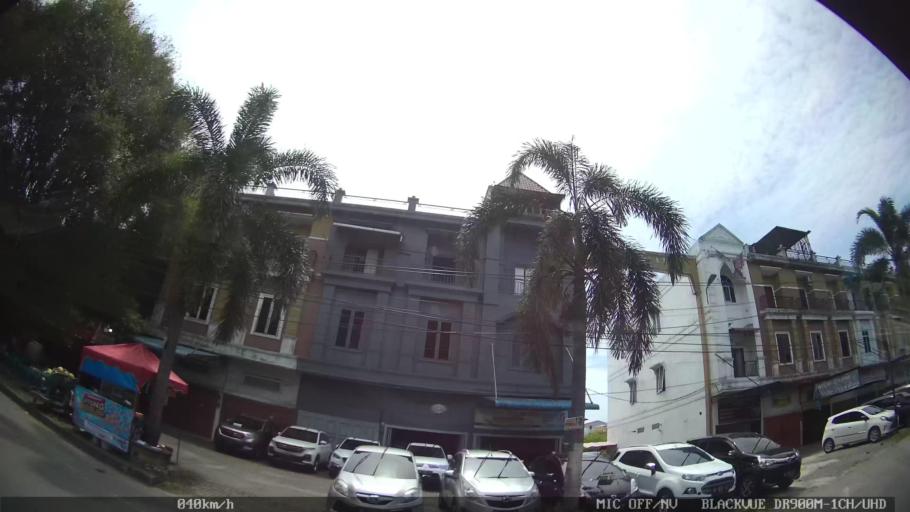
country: ID
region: North Sumatra
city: Sunggal
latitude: 3.5507
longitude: 98.6261
